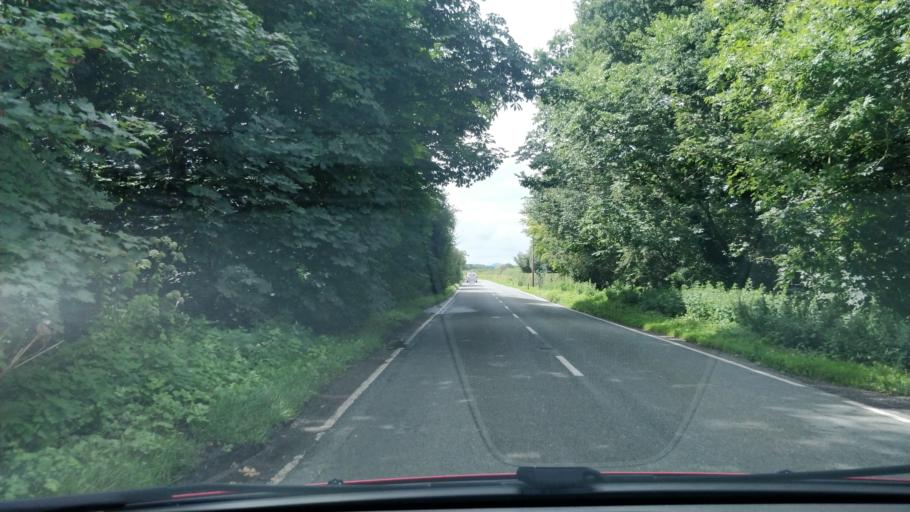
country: GB
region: Wales
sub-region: Wrexham
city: Rossett
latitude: 53.1536
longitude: -2.9425
